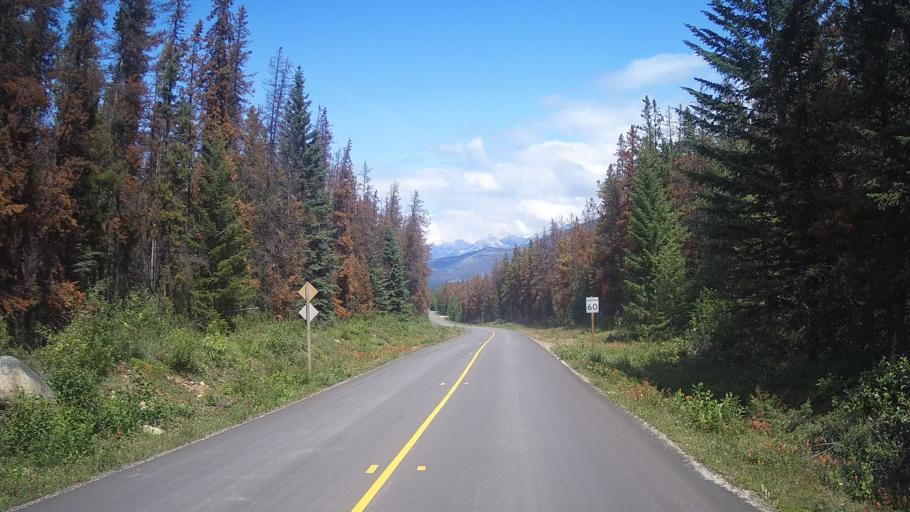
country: CA
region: Alberta
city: Jasper Park Lodge
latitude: 52.7760
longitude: -118.0327
